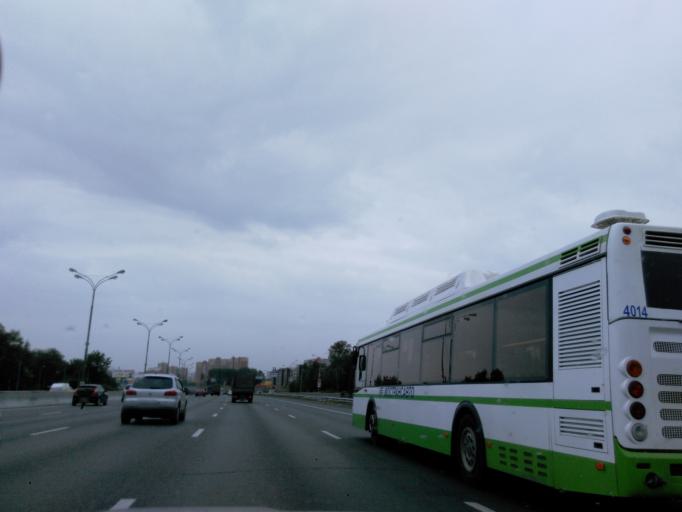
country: RU
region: Moscow
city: Khimki
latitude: 55.8708
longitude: 37.4115
